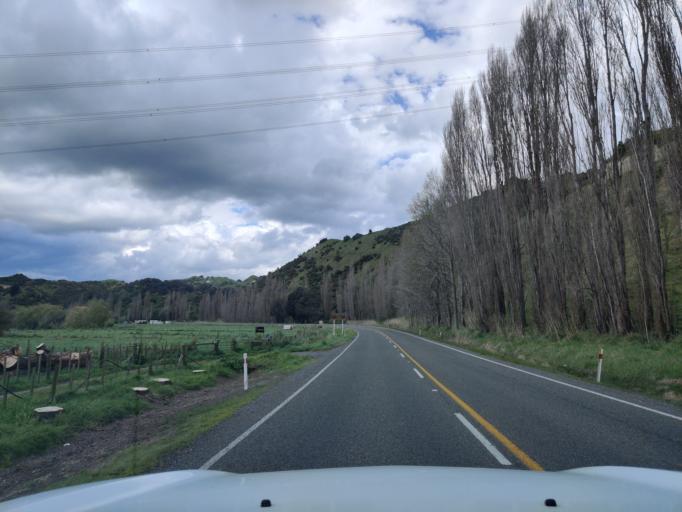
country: NZ
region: Manawatu-Wanganui
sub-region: Wanganui District
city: Wanganui
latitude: -39.8963
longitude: 175.1003
